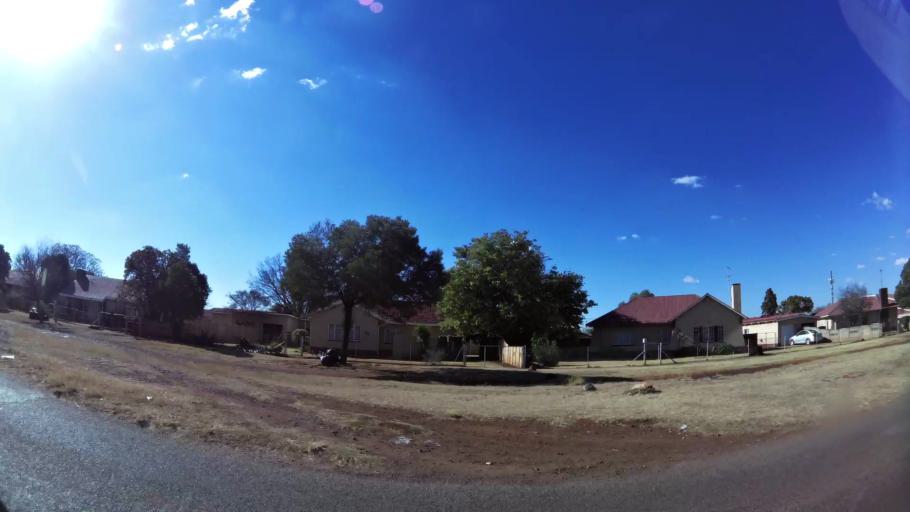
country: ZA
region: Gauteng
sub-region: West Rand District Municipality
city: Carletonville
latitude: -26.3617
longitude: 27.3801
